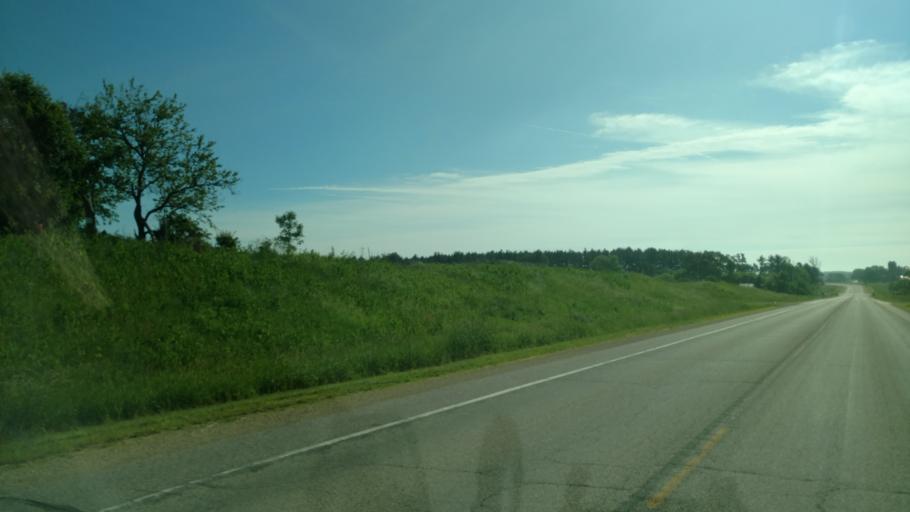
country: US
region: Wisconsin
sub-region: Sauk County
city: Lake Delton
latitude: 43.5474
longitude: -89.8551
